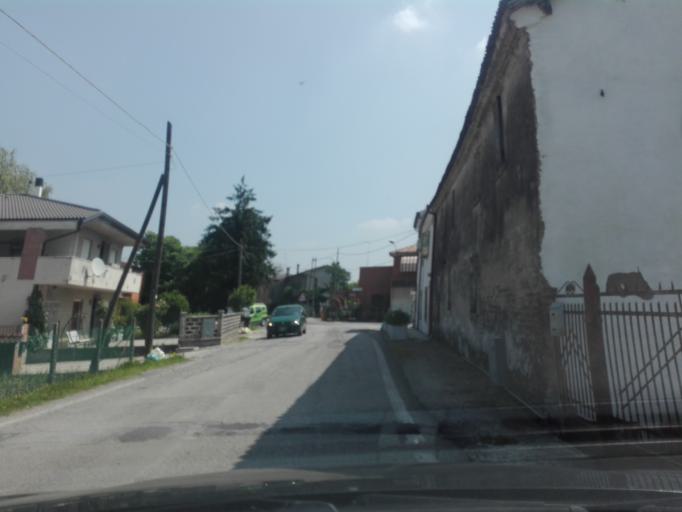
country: IT
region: Veneto
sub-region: Provincia di Rovigo
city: Lama Pezzoli
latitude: 45.0461
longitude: 11.9351
